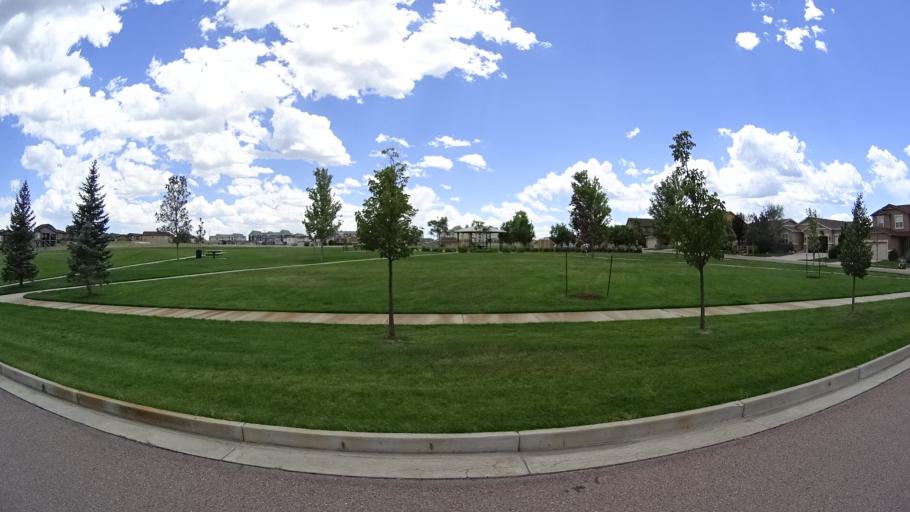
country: US
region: Colorado
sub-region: El Paso County
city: Black Forest
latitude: 38.9484
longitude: -104.7115
